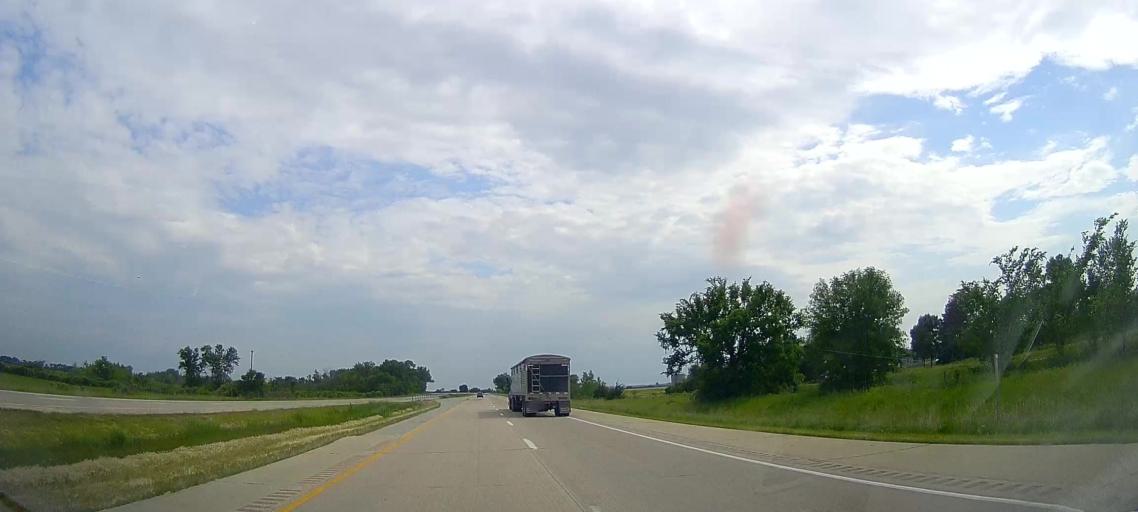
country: US
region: Nebraska
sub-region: Burt County
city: Tekamah
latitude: 41.7922
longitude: -96.0516
